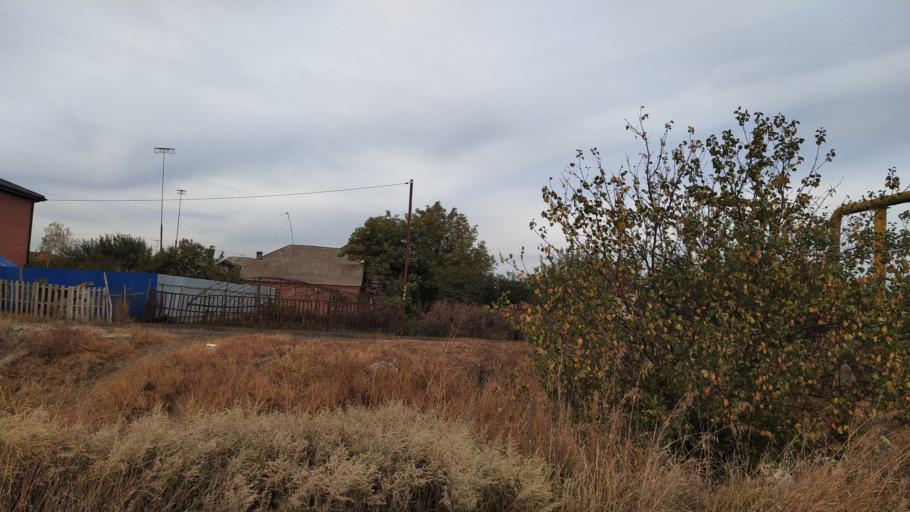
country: RU
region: Rostov
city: Bataysk
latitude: 47.1116
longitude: 39.6807
